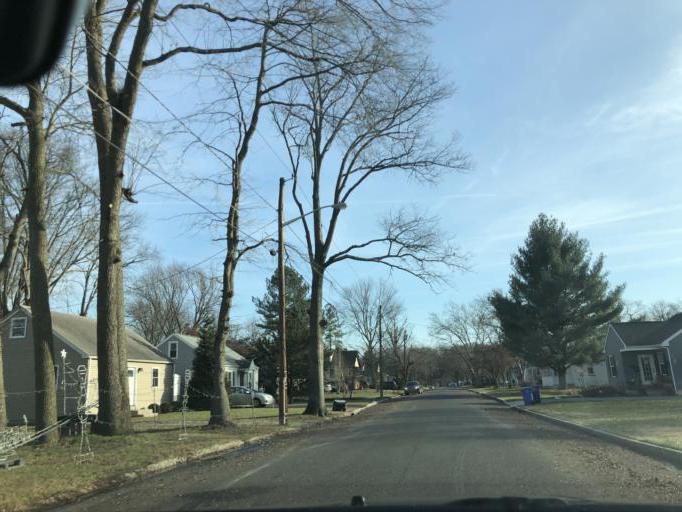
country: US
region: New Jersey
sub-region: Burlington County
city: Maple Shade
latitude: 39.9566
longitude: -74.9796
